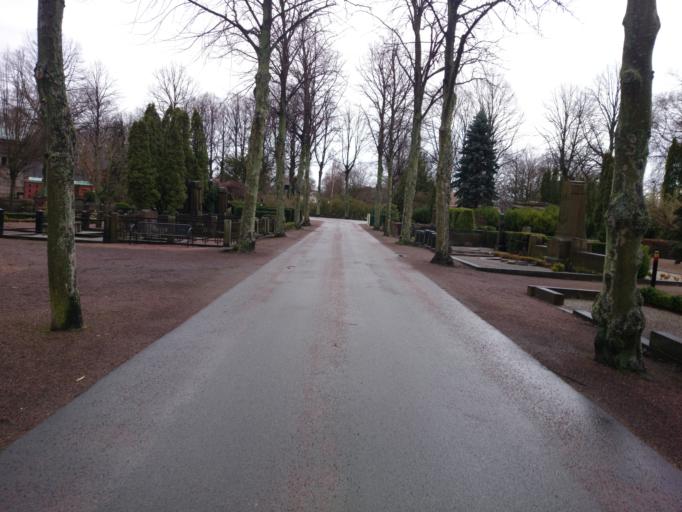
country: SE
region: Skane
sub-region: Malmo
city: Malmoe
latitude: 55.5987
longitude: 13.0185
